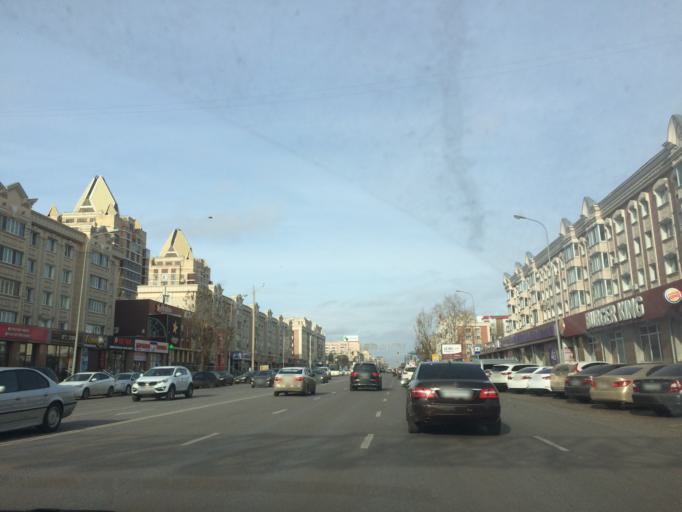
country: KZ
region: Astana Qalasy
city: Astana
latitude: 51.1590
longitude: 71.4293
